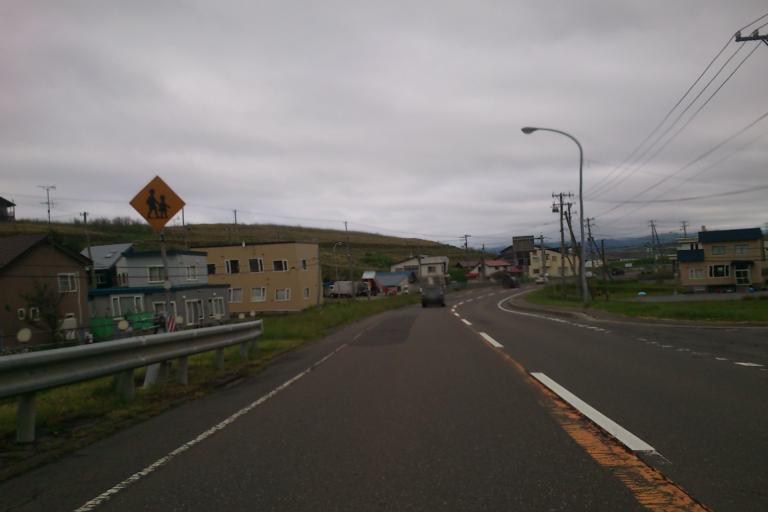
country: JP
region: Hokkaido
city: Ishikari
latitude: 43.3113
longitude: 141.4123
